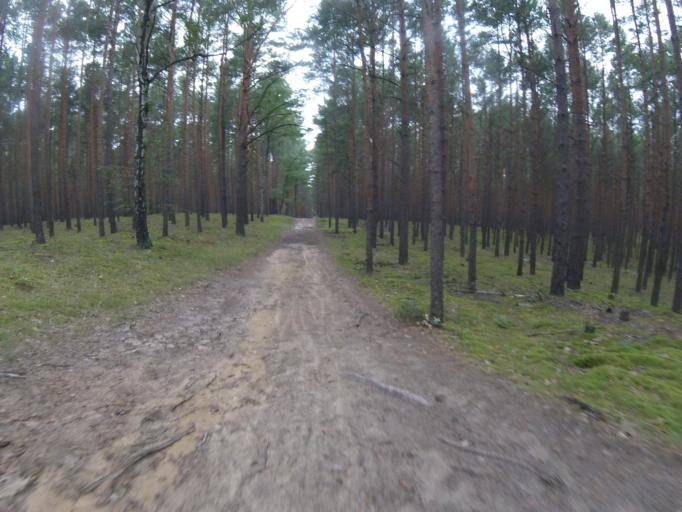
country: DE
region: Brandenburg
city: Gross Koris
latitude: 52.2074
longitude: 13.6586
